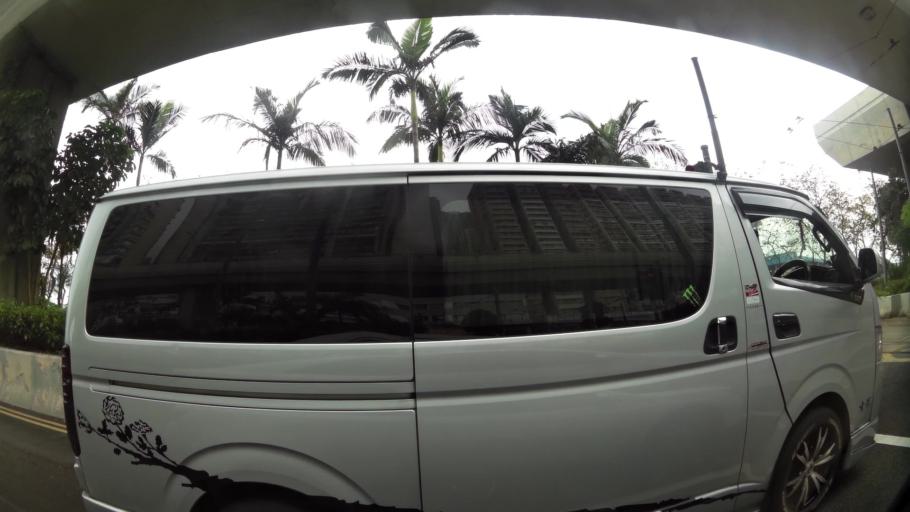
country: HK
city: Hong Kong
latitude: 22.2877
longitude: 114.1338
